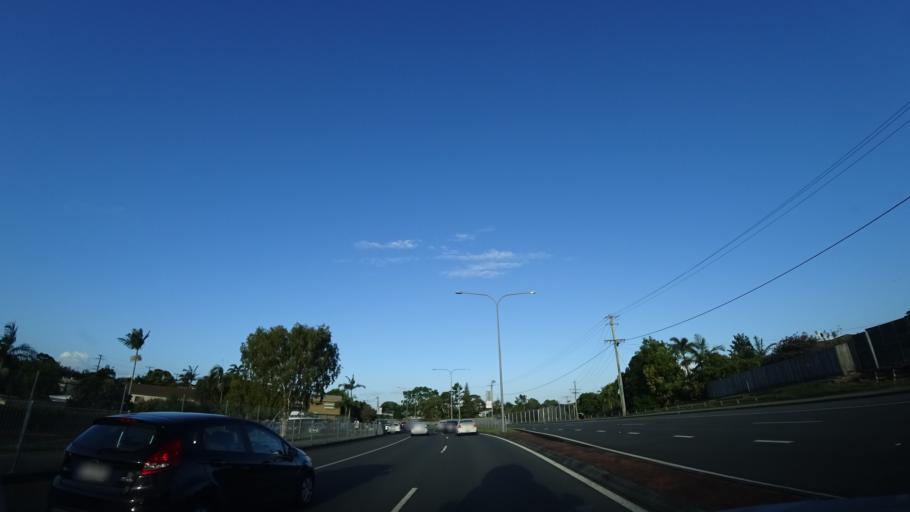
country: AU
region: Queensland
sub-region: Sunshine Coast
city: Buderim
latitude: -26.6548
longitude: 153.0764
